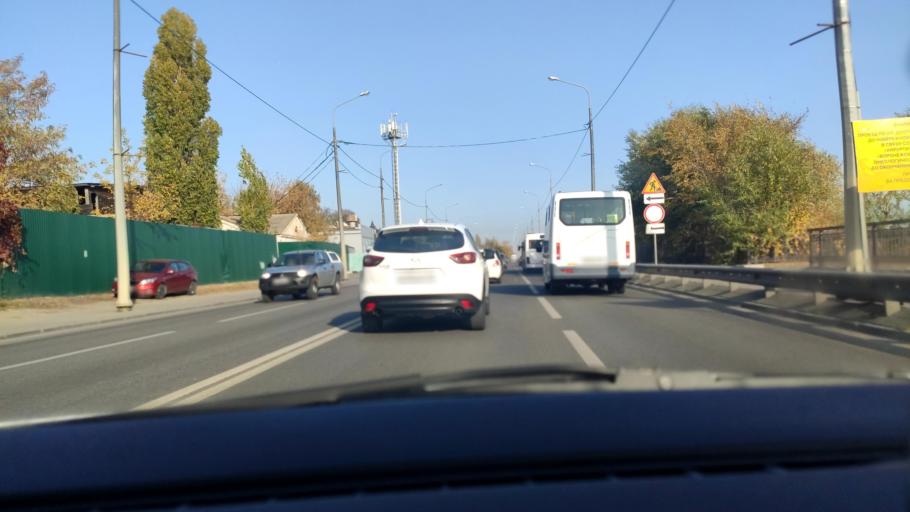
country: RU
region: Voronezj
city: Voronezh
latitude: 51.6731
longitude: 39.2246
